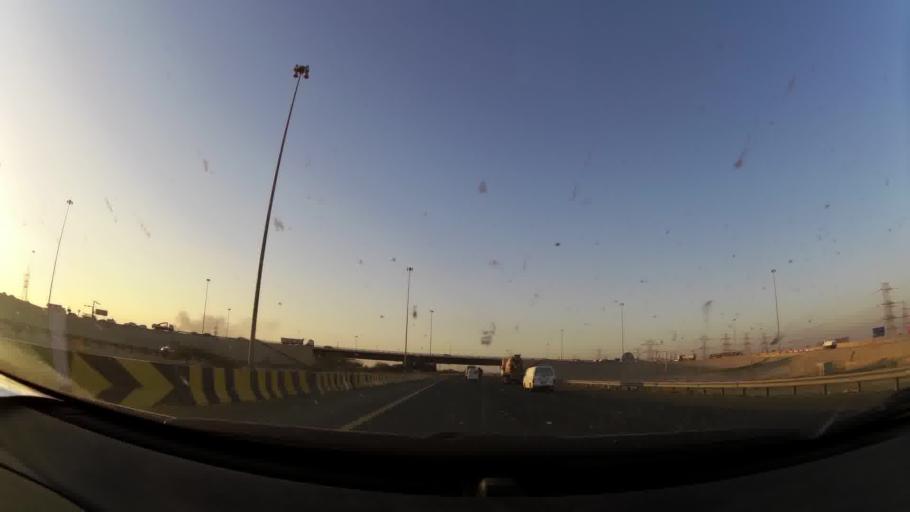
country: KW
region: Al Ahmadi
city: Al Fahahil
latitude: 28.9582
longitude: 48.1238
